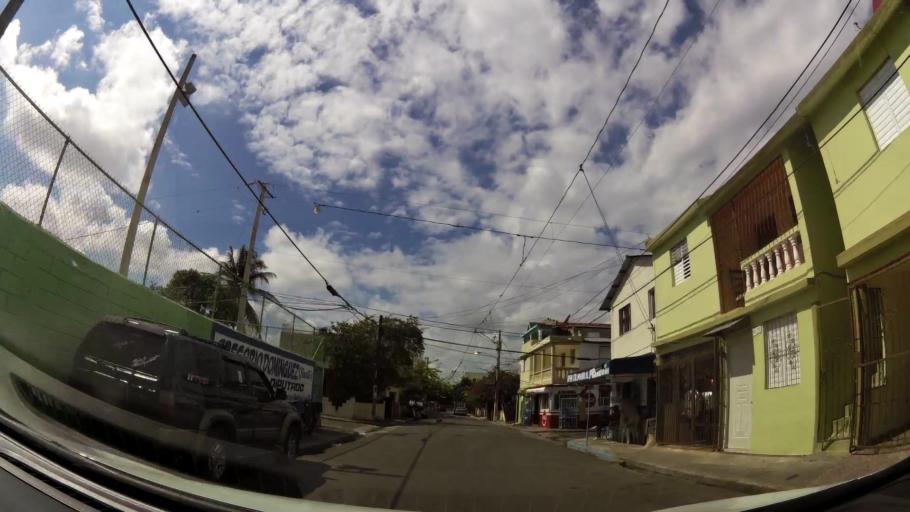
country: DO
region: Santiago
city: Santiago de los Caballeros
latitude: 19.4707
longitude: -70.6973
